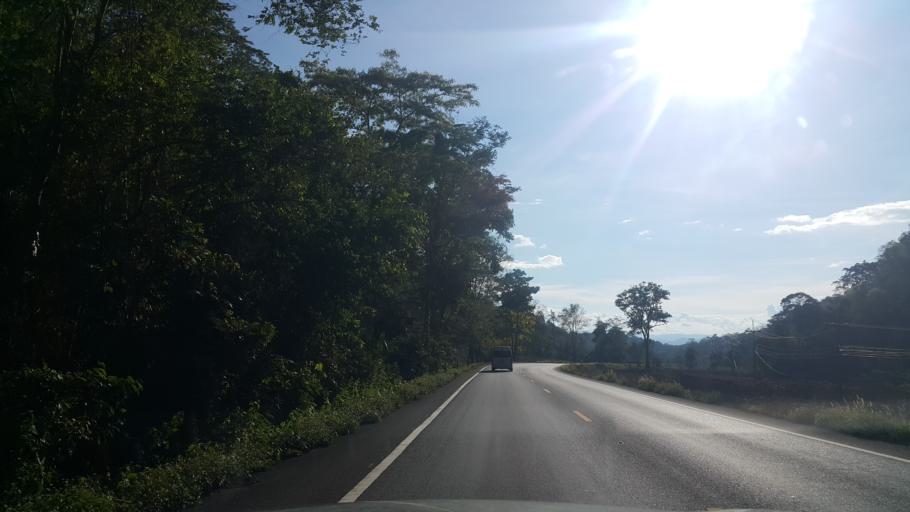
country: TH
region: Lampang
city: Wang Nuea
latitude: 19.0651
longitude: 99.7450
